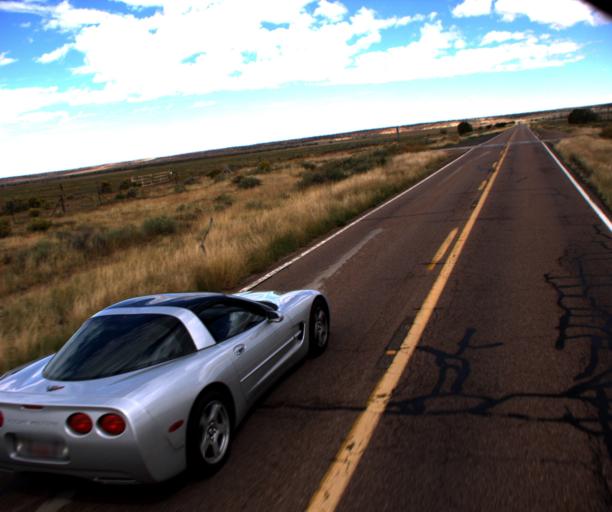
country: US
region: Arizona
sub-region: Navajo County
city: Heber-Overgaard
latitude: 34.6111
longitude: -110.3786
